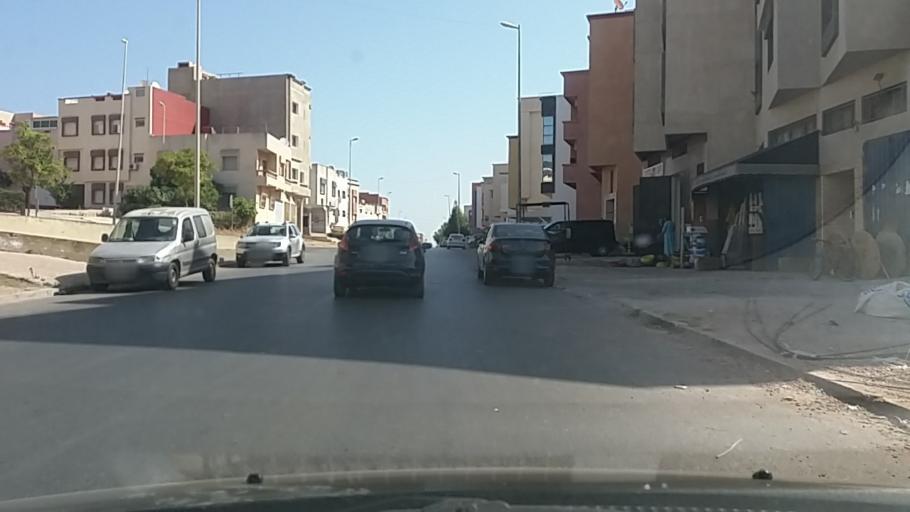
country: MA
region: Gharb-Chrarda-Beni Hssen
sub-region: Kenitra Province
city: Kenitra
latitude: 34.2678
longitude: -6.6122
